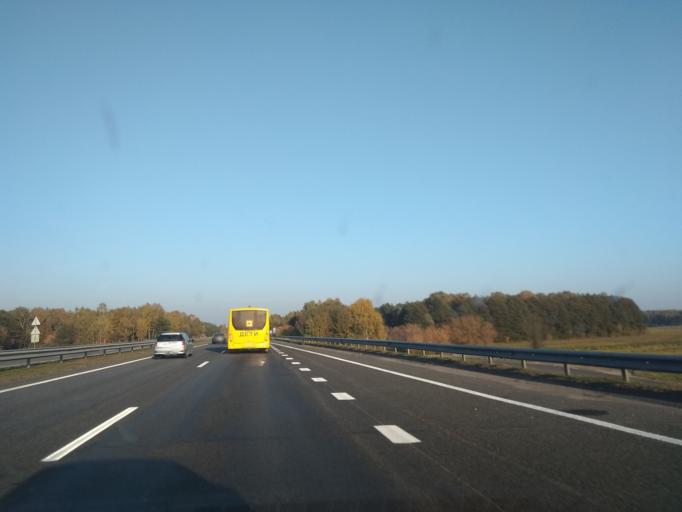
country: BY
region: Brest
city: Zhabinka
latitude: 52.1739
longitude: 24.1479
